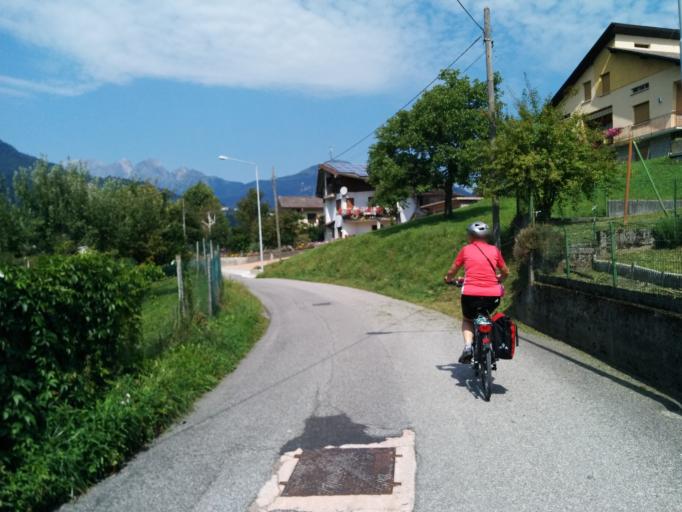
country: IT
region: Friuli Venezia Giulia
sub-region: Provincia di Udine
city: Ovaro
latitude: 46.4814
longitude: 12.8680
